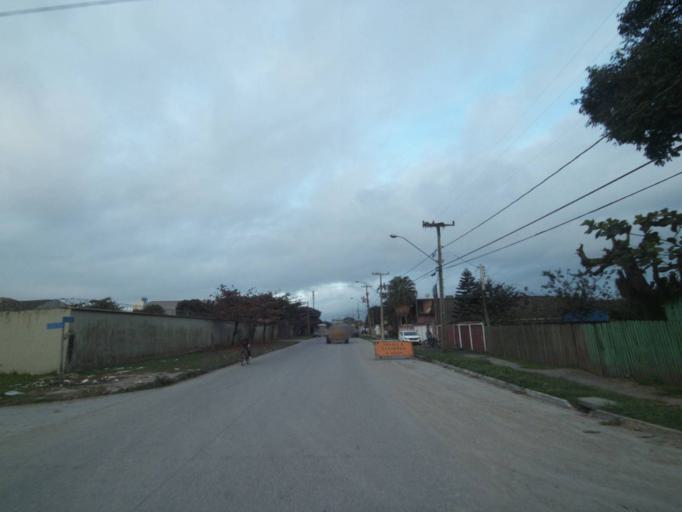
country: BR
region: Parana
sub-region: Paranagua
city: Paranagua
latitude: -25.5087
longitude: -48.5273
